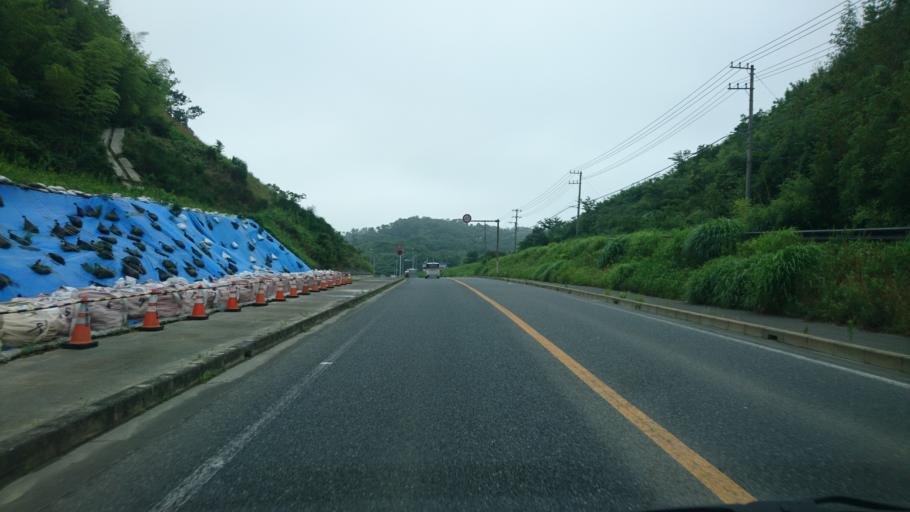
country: JP
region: Chiba
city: Kimitsu
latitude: 35.2547
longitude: 139.8842
